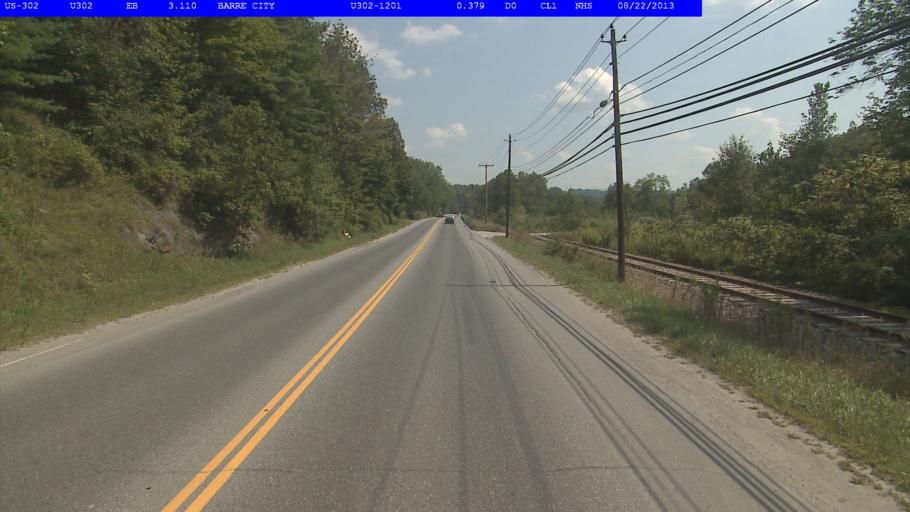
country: US
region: Vermont
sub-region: Washington County
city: Barre
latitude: 44.2135
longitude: -72.5273
